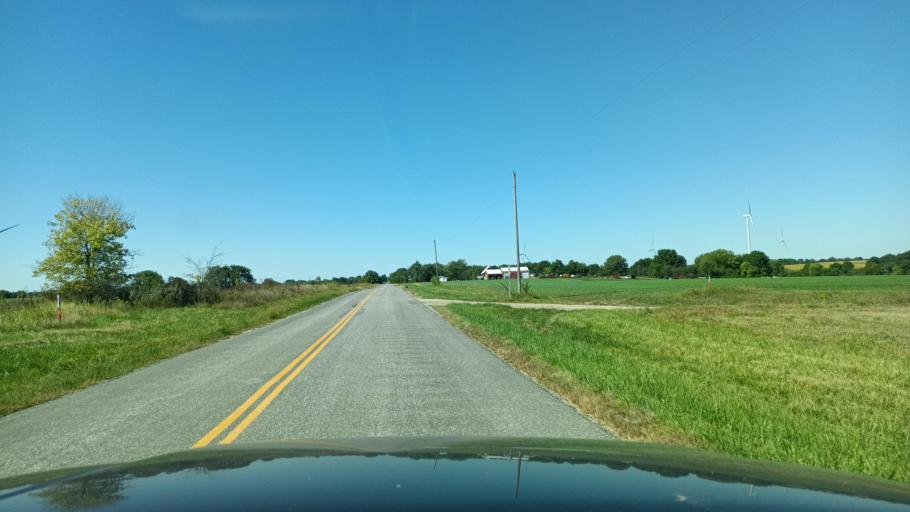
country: US
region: Missouri
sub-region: Adair County
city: Kirksville
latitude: 40.3306
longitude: -92.4973
